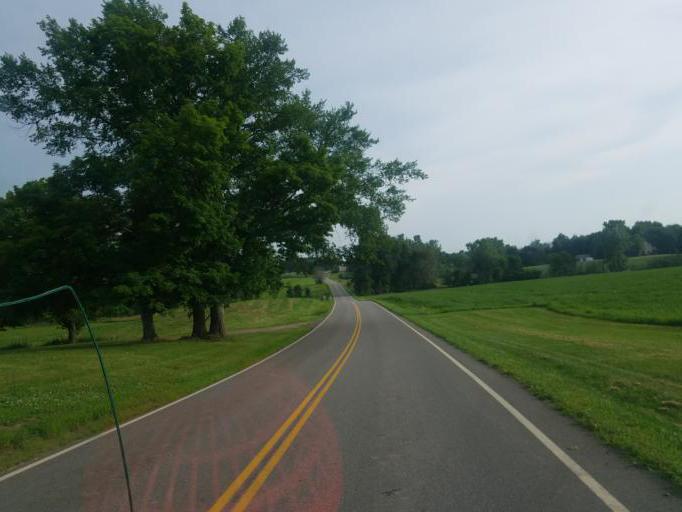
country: US
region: Ohio
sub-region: Ashland County
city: Ashland
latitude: 40.7597
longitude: -82.2671
